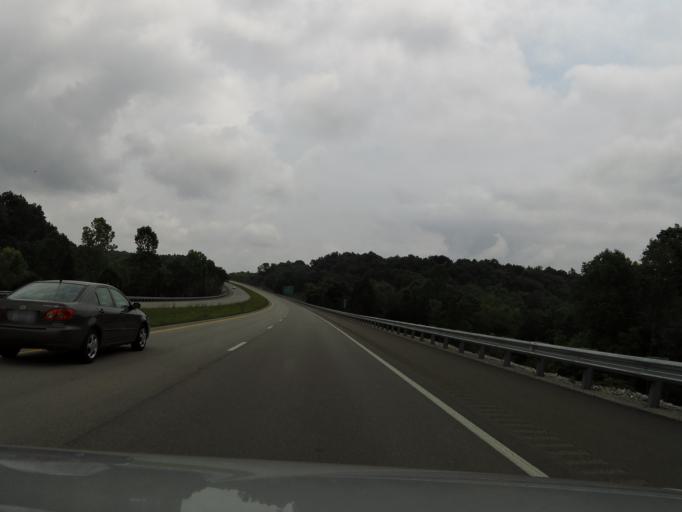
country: US
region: Kentucky
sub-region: Grayson County
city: Leitchfield
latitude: 37.4524
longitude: -86.3244
